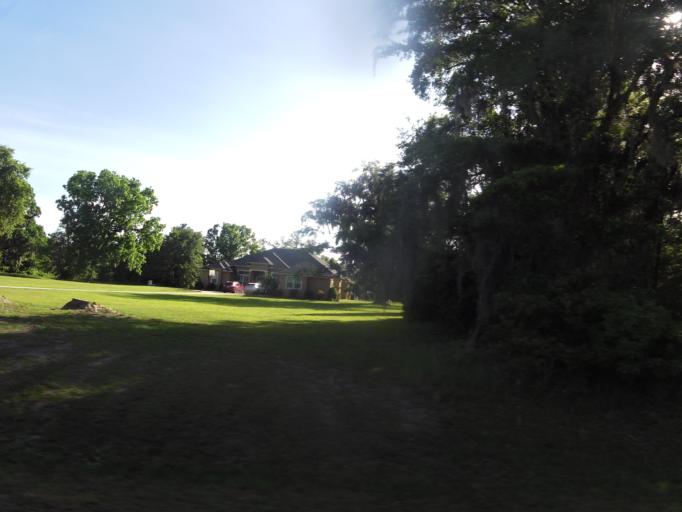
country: US
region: Florida
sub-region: Nassau County
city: Nassau Village-Ratliff
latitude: 30.4680
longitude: -81.8372
